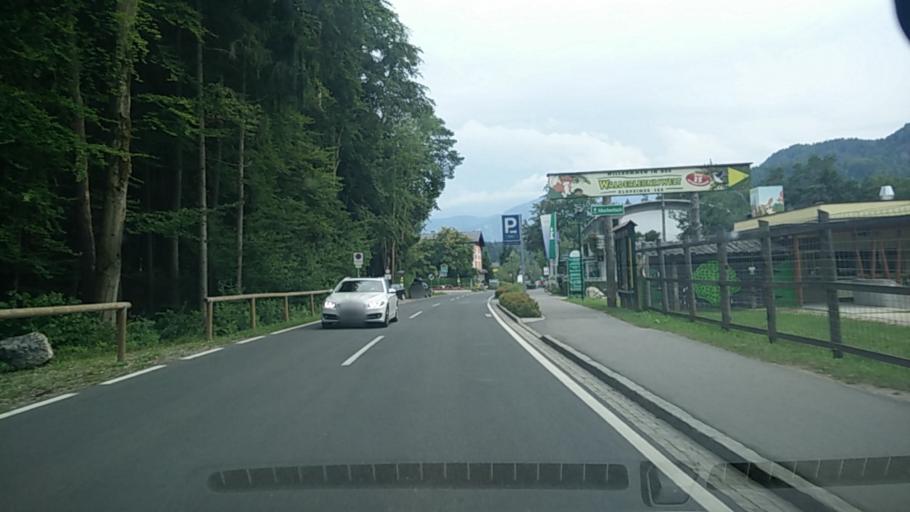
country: AT
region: Carinthia
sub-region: Politischer Bezirk Volkermarkt
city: Eberndorf
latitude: 46.6103
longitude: 14.5758
